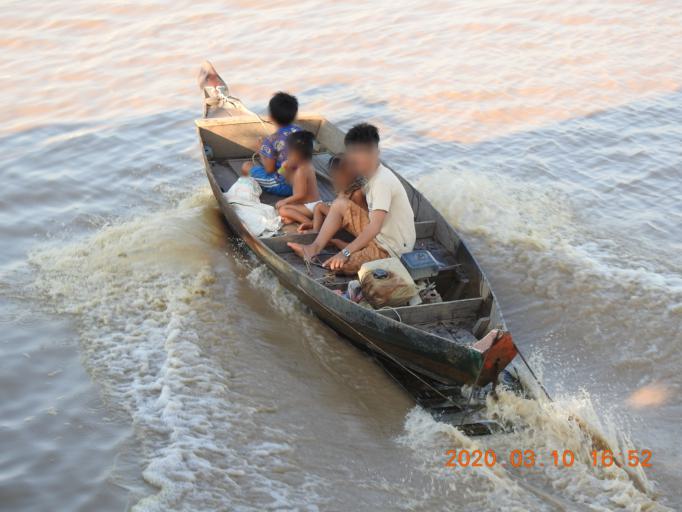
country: KH
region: Siem Reap
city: Siem Reap
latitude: 13.2250
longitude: 103.8262
